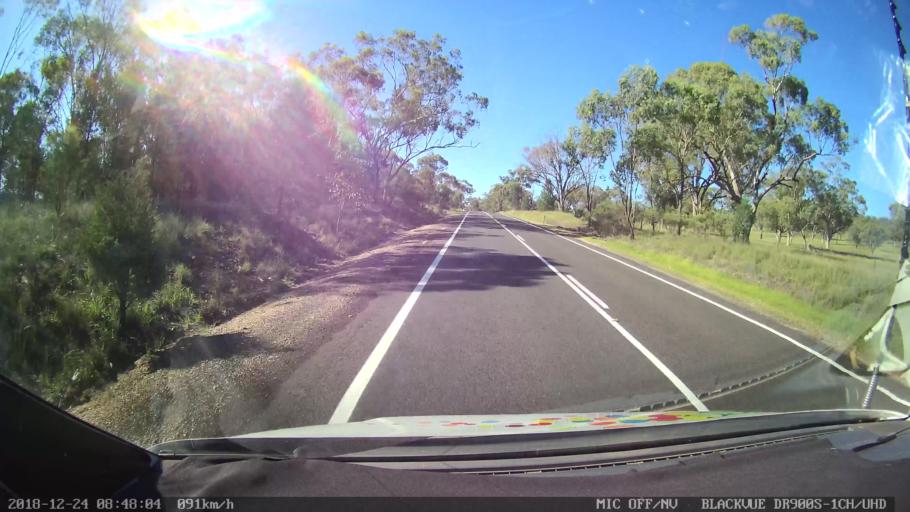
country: AU
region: New South Wales
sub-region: Liverpool Plains
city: Quirindi
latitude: -31.4507
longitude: 150.6461
